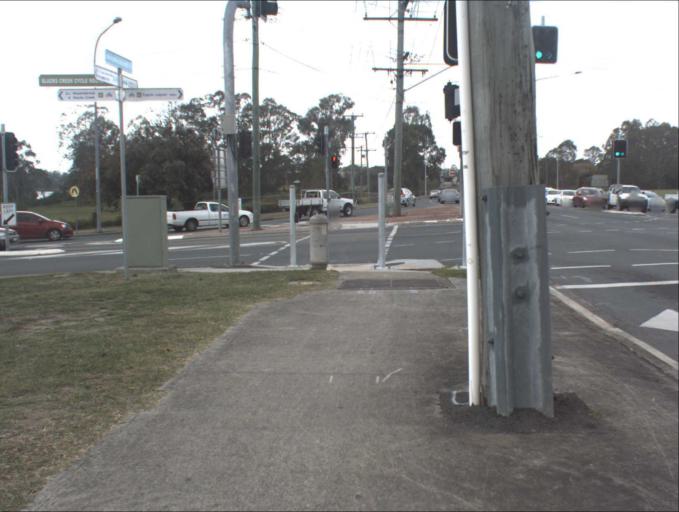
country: AU
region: Queensland
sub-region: Logan
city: Waterford West
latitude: -27.6919
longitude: 153.1360
